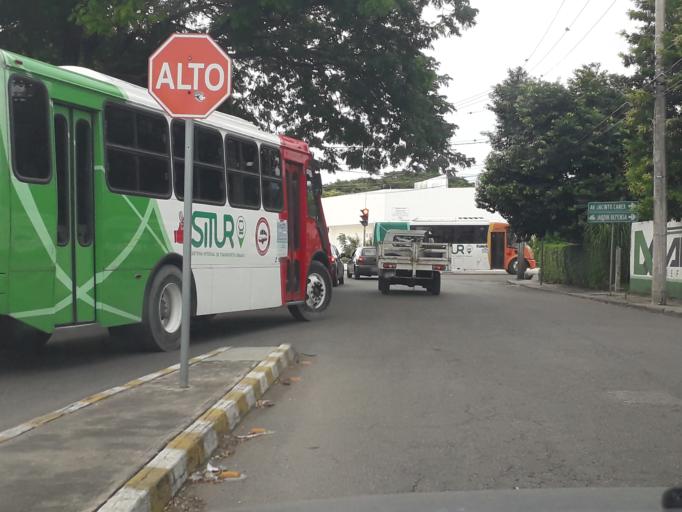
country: MX
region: Yucatan
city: Merida
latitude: 20.9734
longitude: -89.6624
